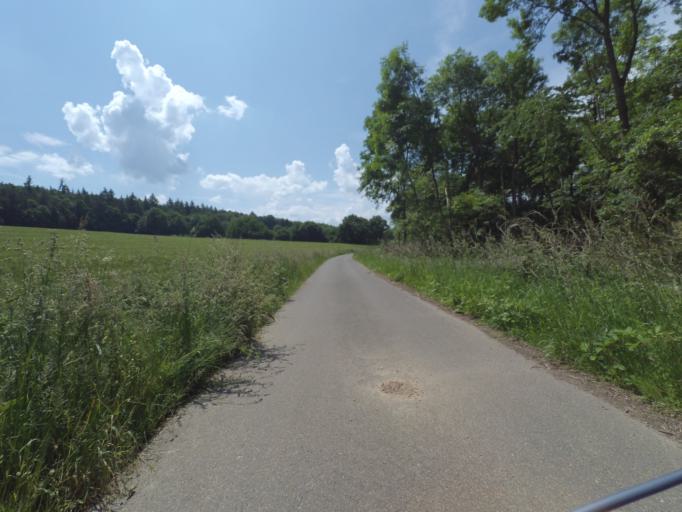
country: DE
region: Rheinland-Pfalz
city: Mermuth
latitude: 50.1662
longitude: 7.4773
